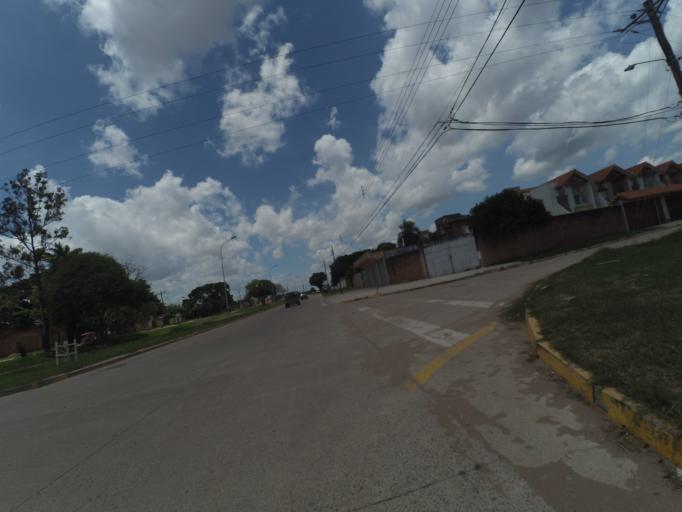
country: BO
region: Santa Cruz
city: Santa Cruz de la Sierra
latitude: -17.7291
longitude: -63.1493
